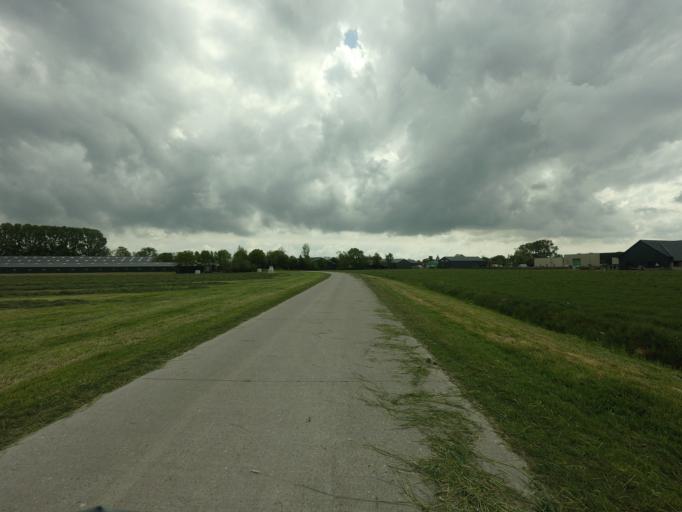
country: NL
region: Friesland
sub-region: Gemeente Littenseradiel
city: Wommels
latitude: 53.1046
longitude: 5.6228
